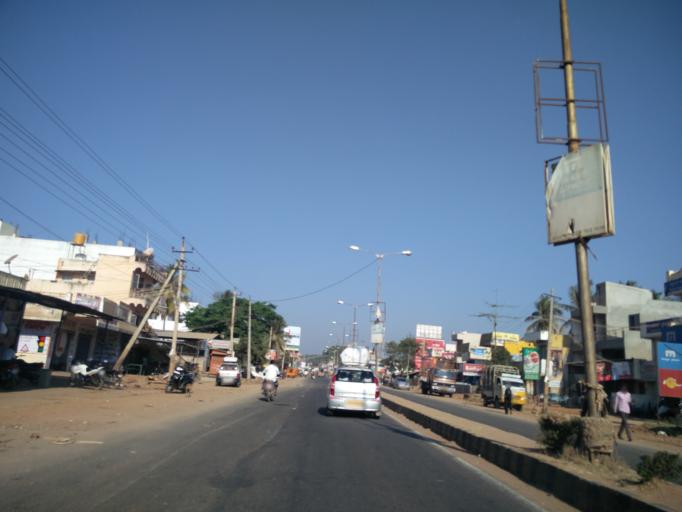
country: IN
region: Karnataka
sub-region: Tumkur
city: Gubbi
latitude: 13.3091
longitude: 76.9453
